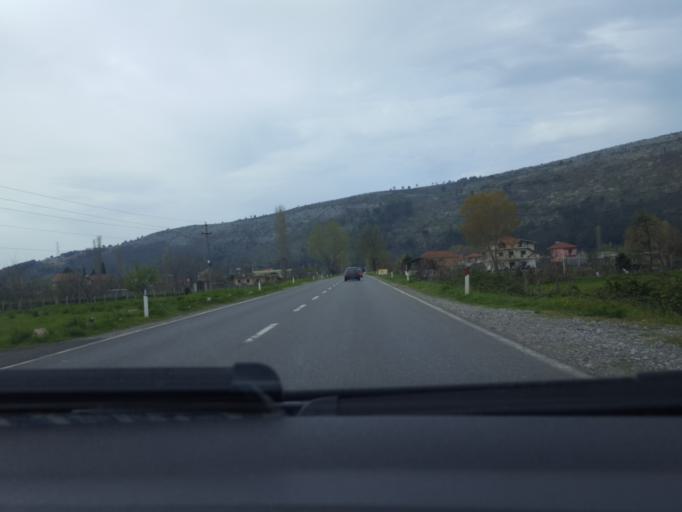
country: AL
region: Lezhe
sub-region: Rrethi i Lezhes
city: Balldreni i Ri
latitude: 41.8102
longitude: 19.6352
